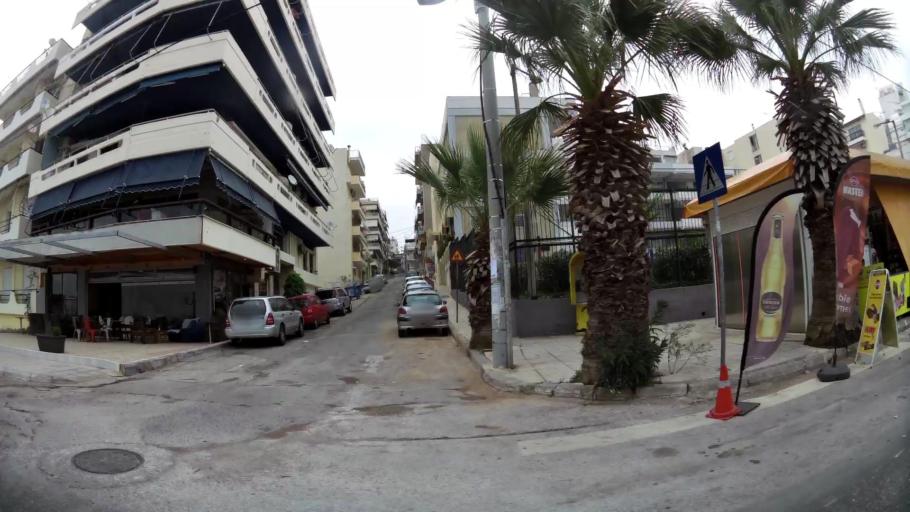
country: GR
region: Attica
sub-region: Nomos Attikis
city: Piraeus
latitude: 37.9311
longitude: 23.6273
